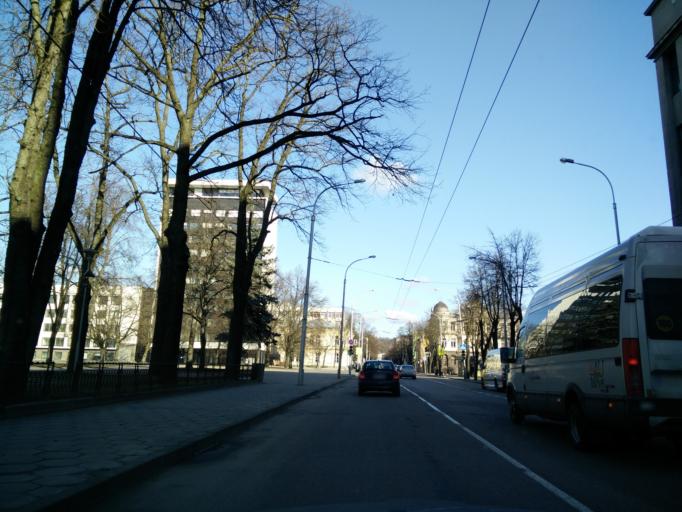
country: LT
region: Kauno apskritis
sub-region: Kaunas
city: Kaunas
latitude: 54.8991
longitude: 23.9125
